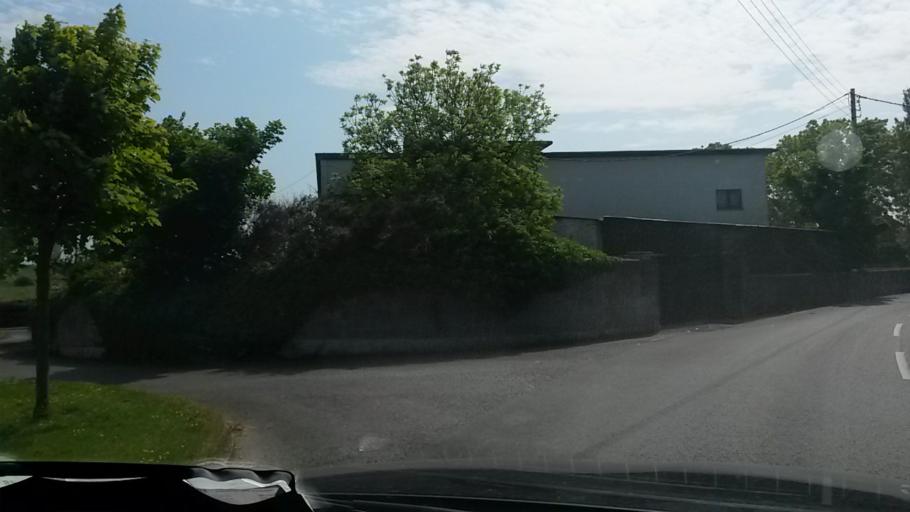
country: IE
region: Leinster
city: Portraine
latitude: 53.4938
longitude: -6.1114
